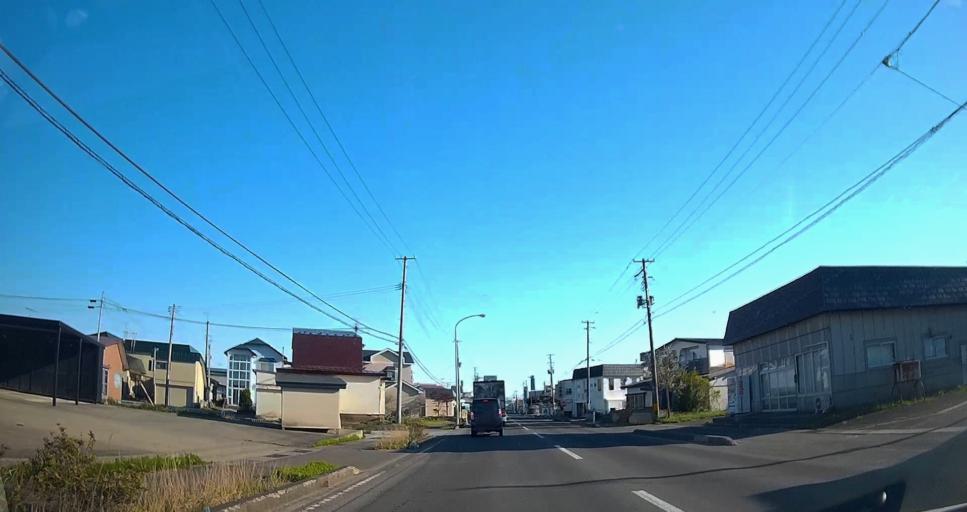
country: JP
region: Aomori
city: Mutsu
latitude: 41.2991
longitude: 141.2217
